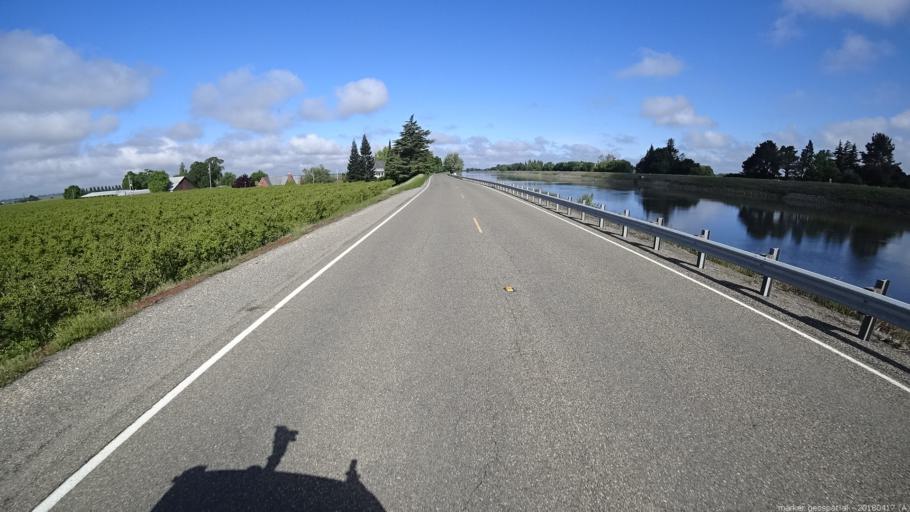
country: US
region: California
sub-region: Sacramento County
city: Walnut Grove
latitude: 38.2688
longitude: -121.5334
